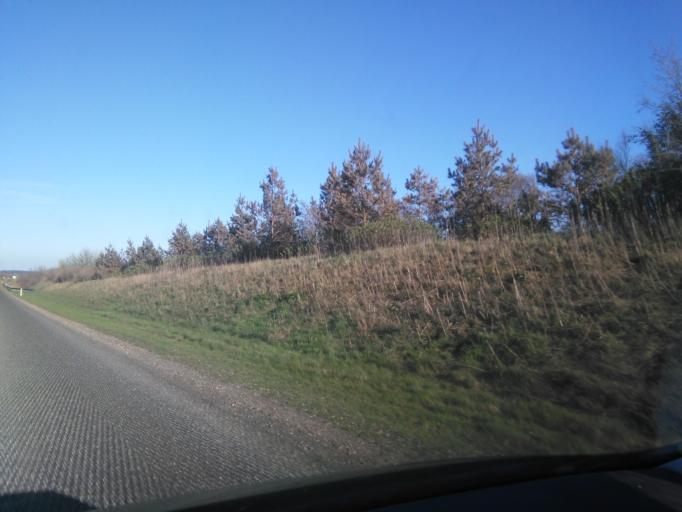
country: DK
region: Central Jutland
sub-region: Ringkobing-Skjern Kommune
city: Videbaek
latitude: 56.0987
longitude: 8.6188
